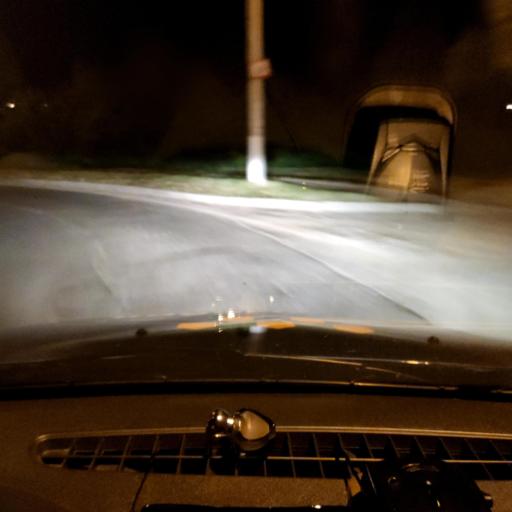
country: RU
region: Belgorod
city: Mayskiy
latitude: 50.5160
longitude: 36.4630
